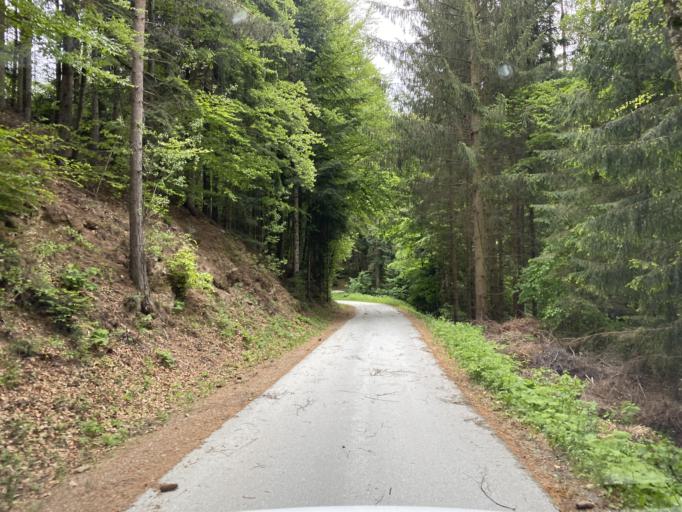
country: AT
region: Styria
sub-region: Politischer Bezirk Weiz
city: Koglhof
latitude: 47.3244
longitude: 15.7012
